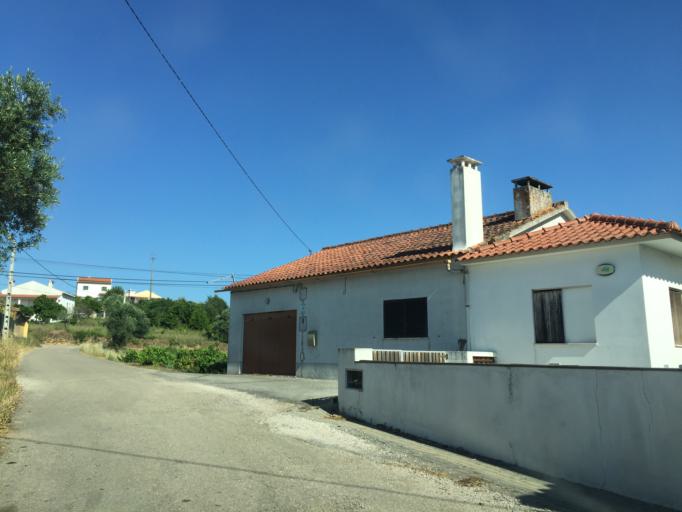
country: PT
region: Santarem
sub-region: Tomar
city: Tomar
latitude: 39.5970
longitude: -8.3244
